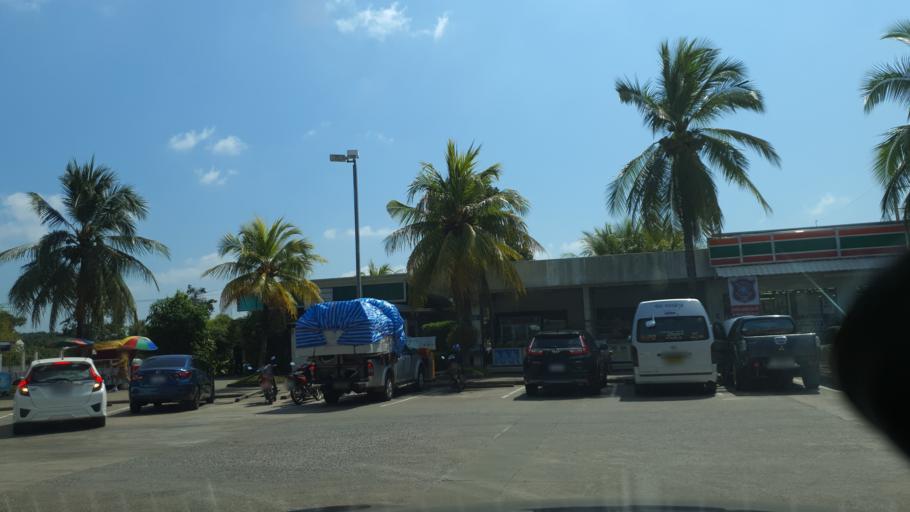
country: TH
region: Krabi
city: Nuea Khlong
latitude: 8.0749
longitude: 98.9952
